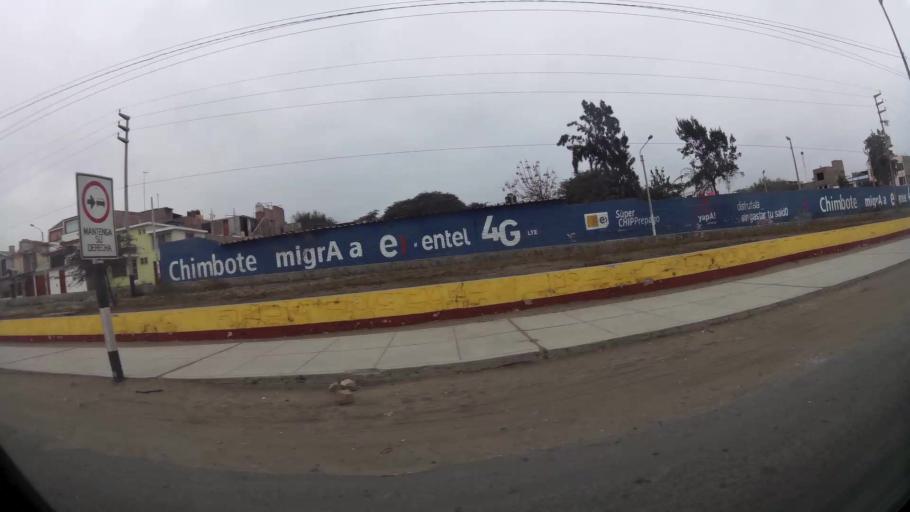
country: PE
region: Ancash
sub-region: Provincia de Santa
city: Chimbote
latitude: -9.0575
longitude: -78.5904
